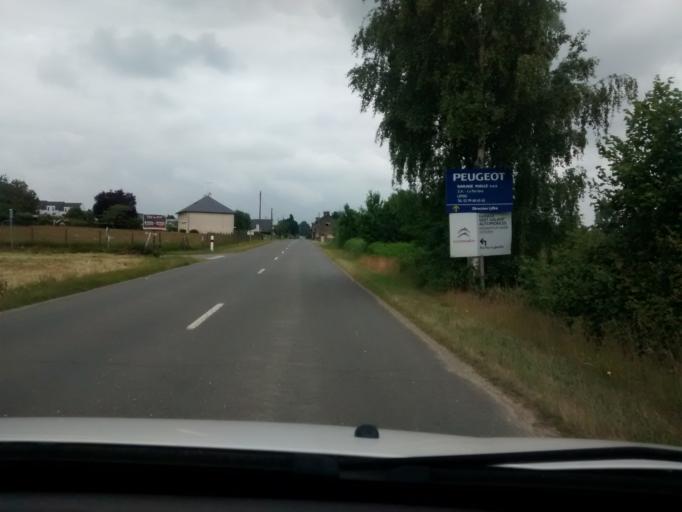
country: FR
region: Brittany
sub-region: Departement d'Ille-et-Vilaine
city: Liffre
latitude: 48.2013
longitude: -1.5103
